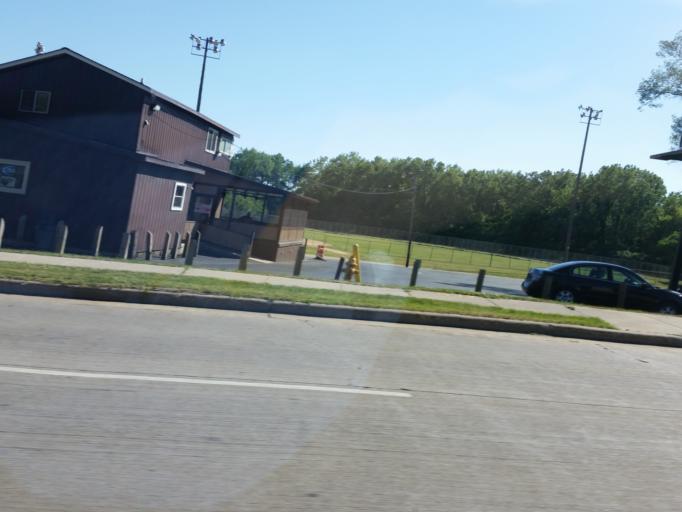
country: US
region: Wisconsin
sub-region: Rock County
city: Beloit
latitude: 42.4979
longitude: -89.0206
